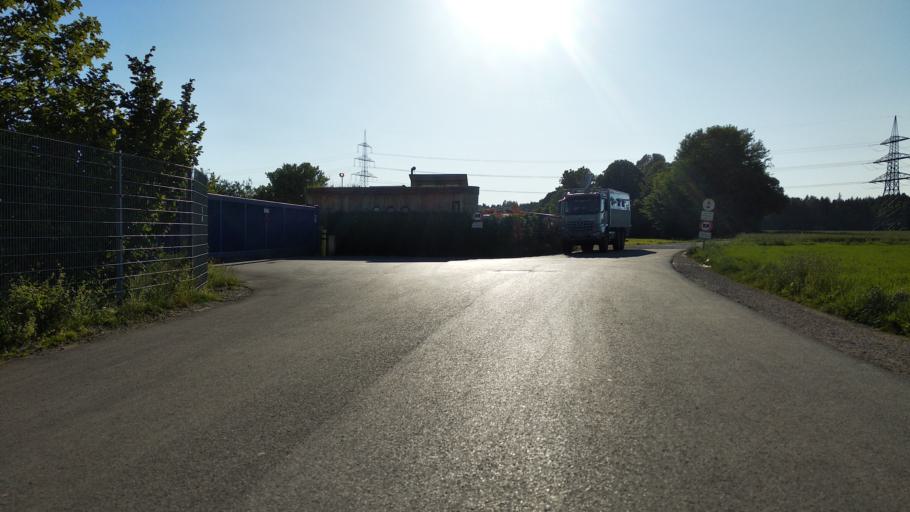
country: DE
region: Bavaria
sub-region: Upper Bavaria
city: Zorneding
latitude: 48.0951
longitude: 11.8208
